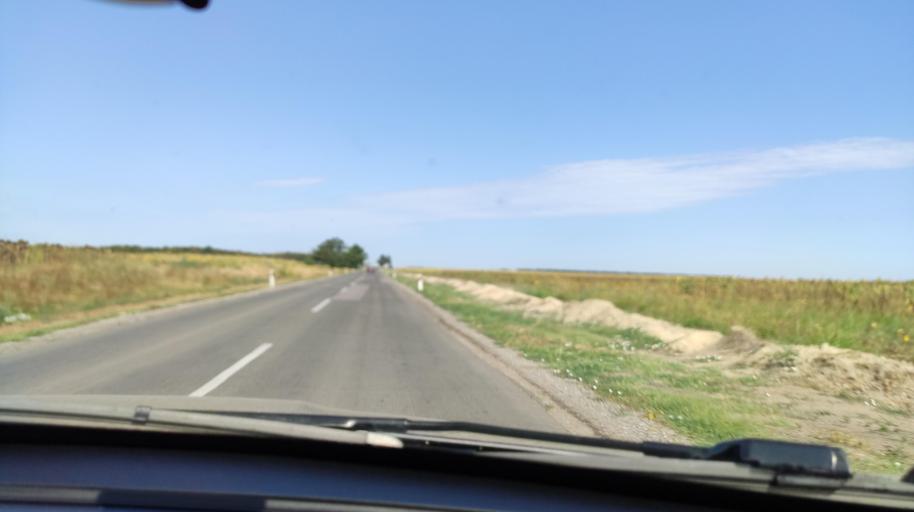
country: RS
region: Autonomna Pokrajina Vojvodina
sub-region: Severnobacki Okrug
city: Backa Topola
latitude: 45.8330
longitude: 19.5871
